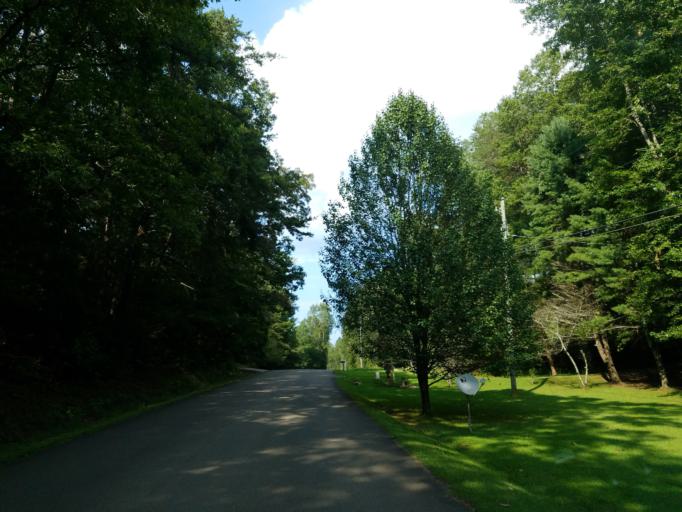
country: US
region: Georgia
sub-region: Fannin County
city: Blue Ridge
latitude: 34.7830
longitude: -84.3954
